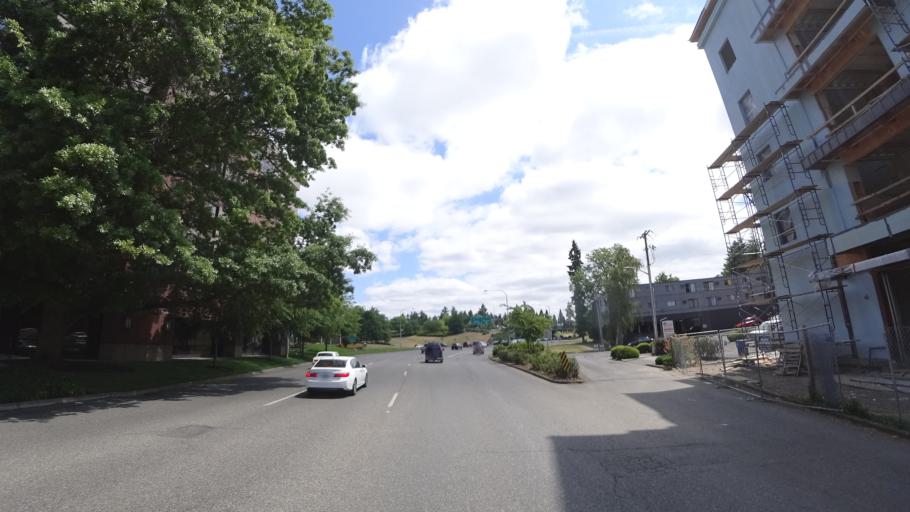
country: US
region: Washington
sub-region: Clark County
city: Vancouver
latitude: 45.6318
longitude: -122.6679
